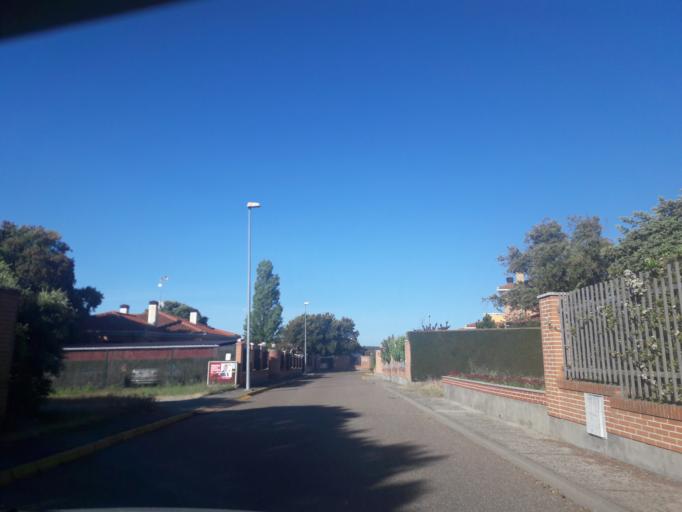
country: ES
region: Castille and Leon
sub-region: Provincia de Salamanca
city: Martinamor
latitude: 40.8043
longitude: -5.6345
